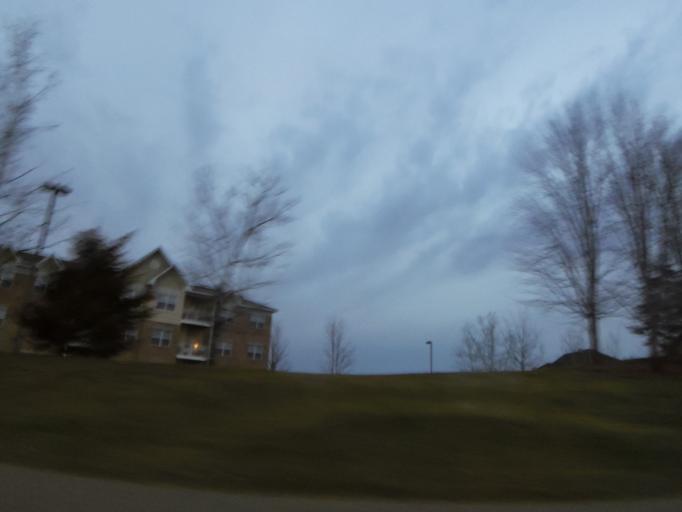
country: US
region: Wisconsin
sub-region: Saint Croix County
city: Hudson
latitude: 44.9492
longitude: -92.7084
